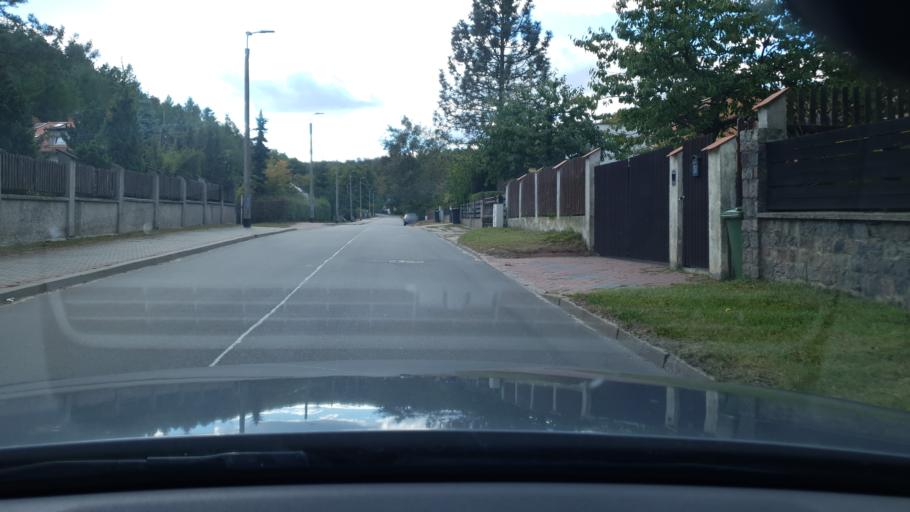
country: PL
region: Pomeranian Voivodeship
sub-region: Powiat wejherowski
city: Reda
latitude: 54.5950
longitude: 18.3402
